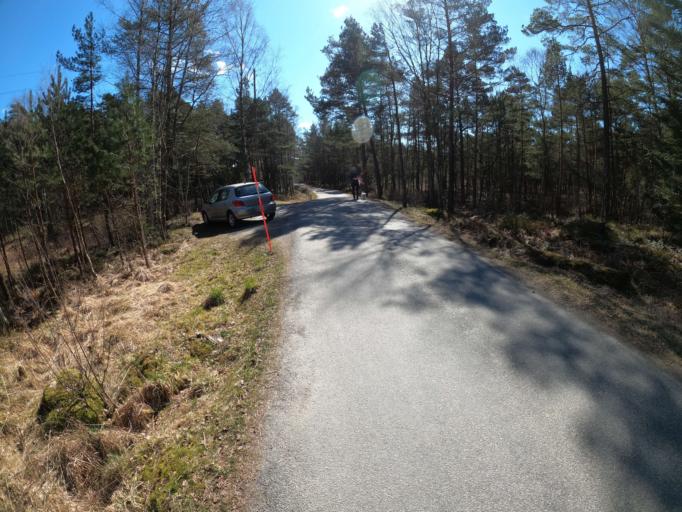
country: SE
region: Vaestra Goetaland
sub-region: Harryda Kommun
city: Molnlycke
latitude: 57.6332
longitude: 12.1188
